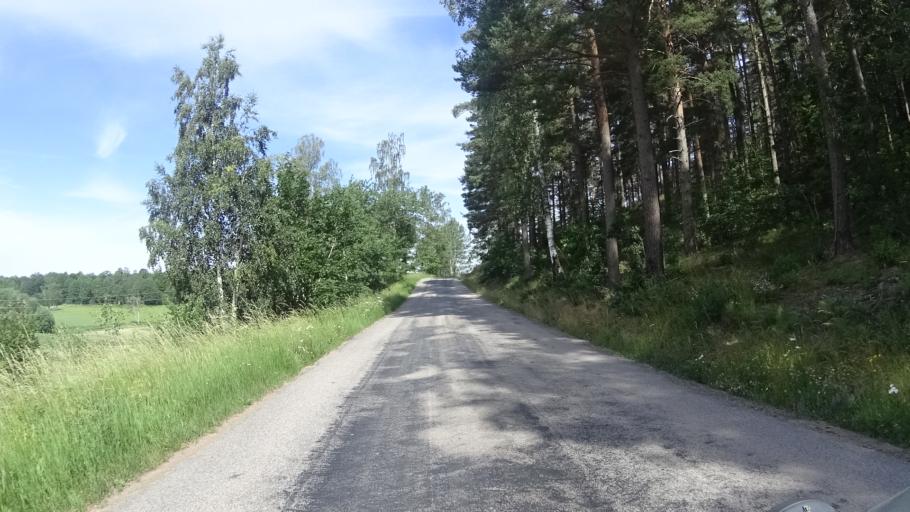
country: SE
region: Kalmar
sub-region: Vasterviks Kommun
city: Overum
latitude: 57.8735
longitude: 16.1754
